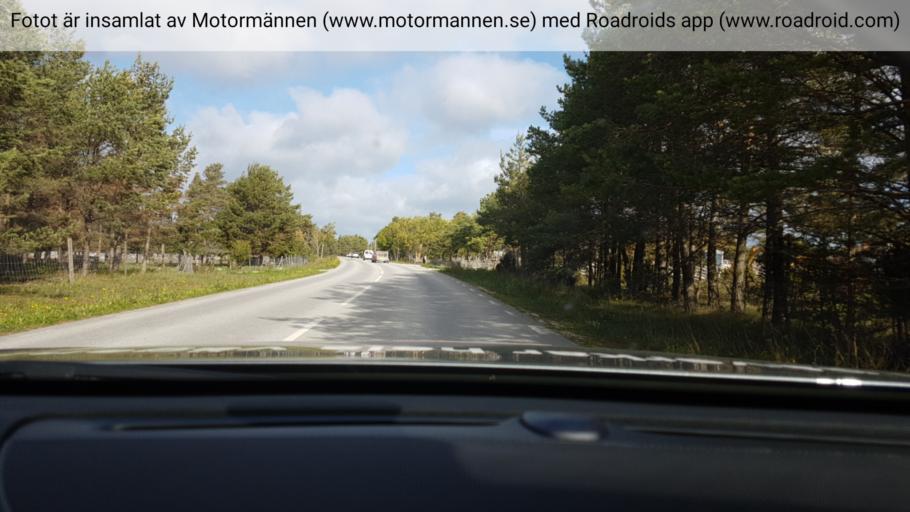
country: SE
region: Gotland
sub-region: Gotland
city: Slite
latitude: 57.8945
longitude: 19.0931
